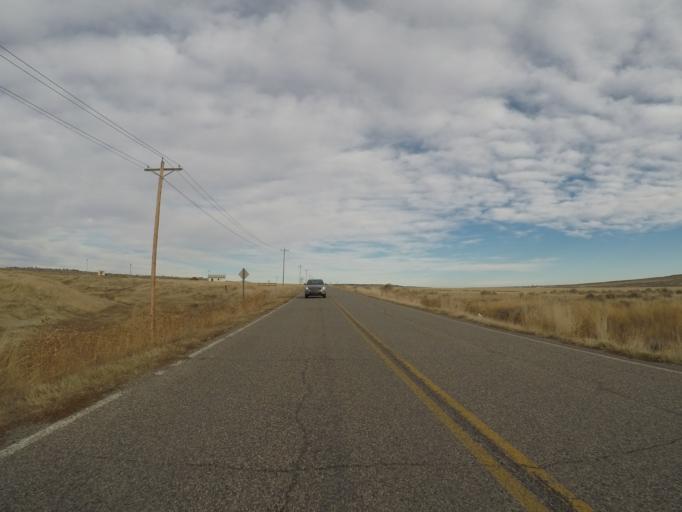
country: US
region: Montana
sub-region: Yellowstone County
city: Laurel
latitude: 45.7819
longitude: -108.7351
